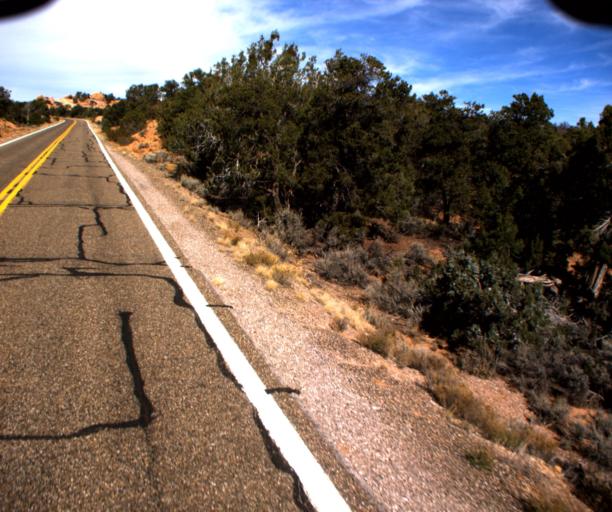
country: US
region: Arizona
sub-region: Navajo County
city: Kayenta
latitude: 36.6661
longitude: -110.5288
